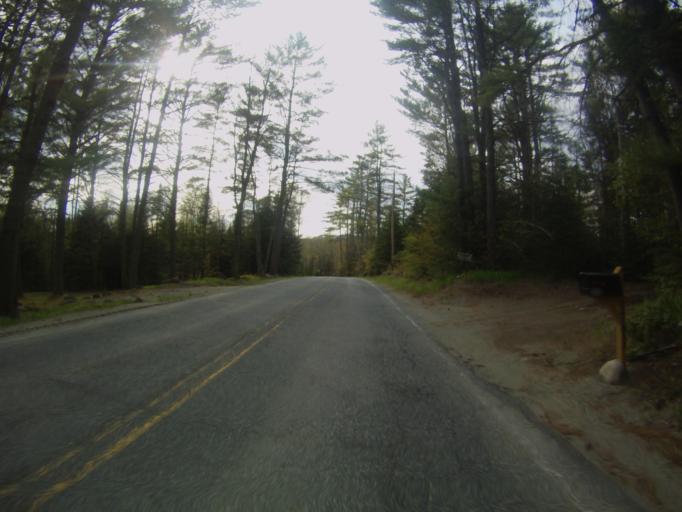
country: US
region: New York
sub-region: Warren County
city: Warrensburg
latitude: 43.8392
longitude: -73.8482
